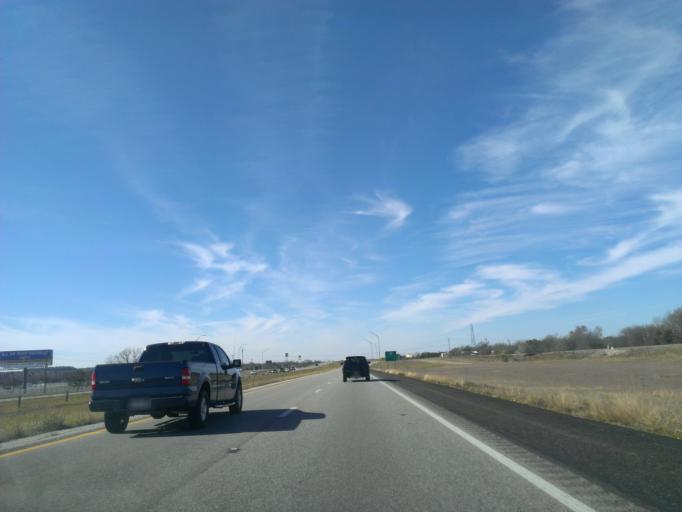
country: US
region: Texas
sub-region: Bell County
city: Nolanville
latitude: 31.0735
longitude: -97.5976
